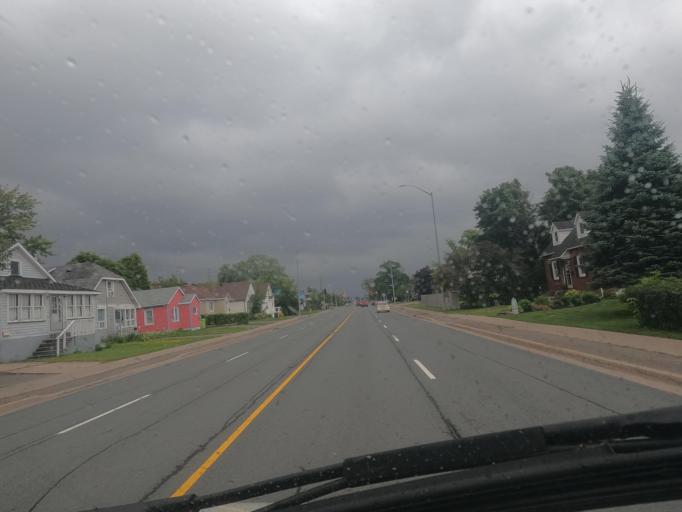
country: CA
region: Ontario
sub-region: Algoma
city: Sault Ste. Marie
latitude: 46.5094
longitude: -84.3100
